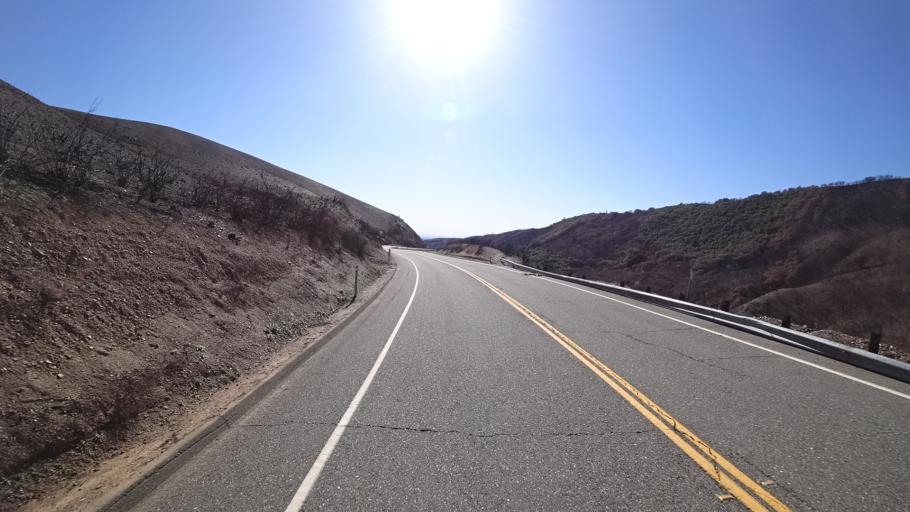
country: US
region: California
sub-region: Tehama County
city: Rancho Tehama Reserve
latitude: 39.6626
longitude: -122.6600
